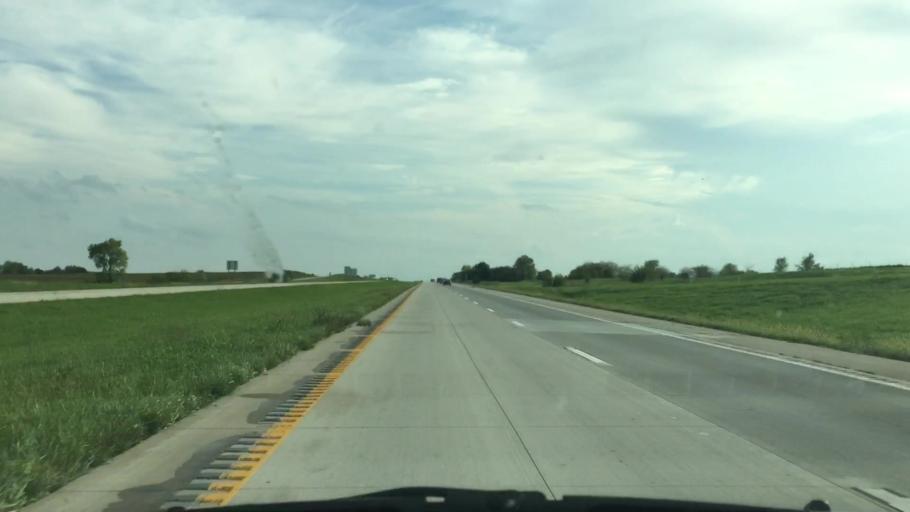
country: US
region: Missouri
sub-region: Harrison County
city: Bethany
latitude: 40.0758
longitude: -94.0936
